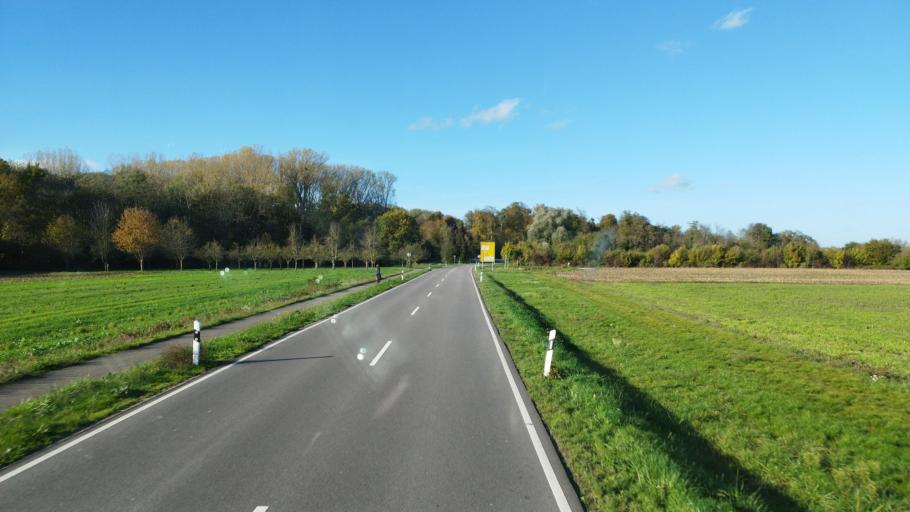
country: DE
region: Rheinland-Pfalz
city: Jockgrim
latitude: 49.0761
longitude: 8.2783
